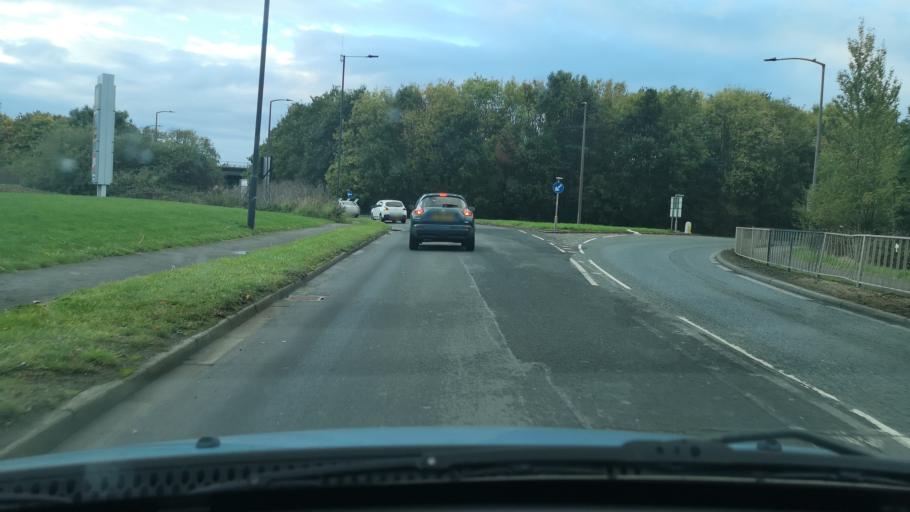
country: GB
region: England
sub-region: Doncaster
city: Hatfield
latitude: 53.6175
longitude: -0.9762
